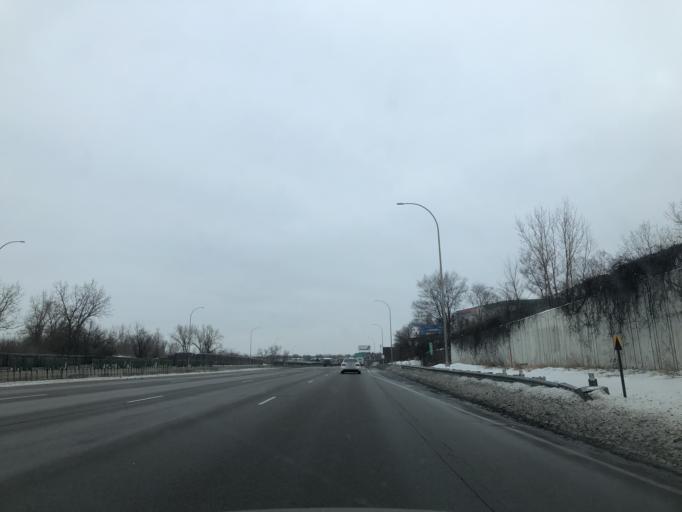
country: US
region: Minnesota
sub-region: Anoka County
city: Columbia Heights
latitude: 45.0375
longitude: -93.2858
